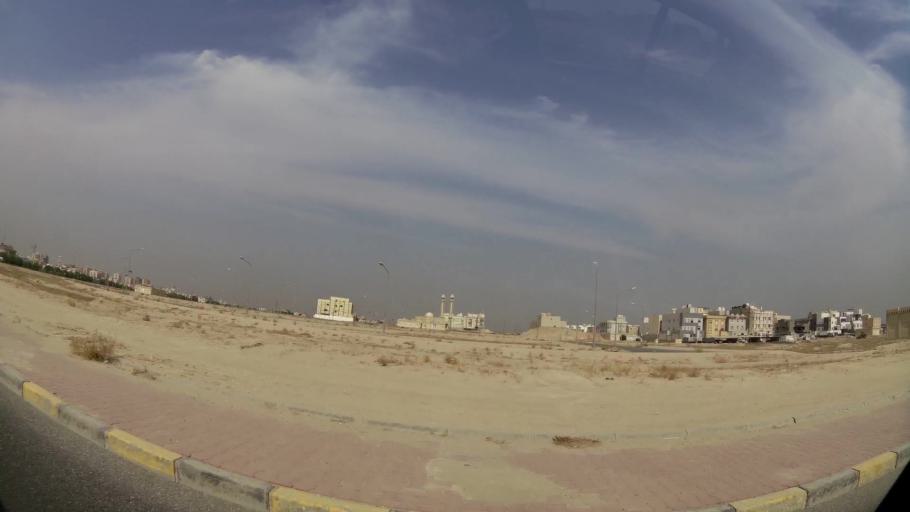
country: KW
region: Al Farwaniyah
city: Janub as Surrah
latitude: 29.2890
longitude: 47.9867
